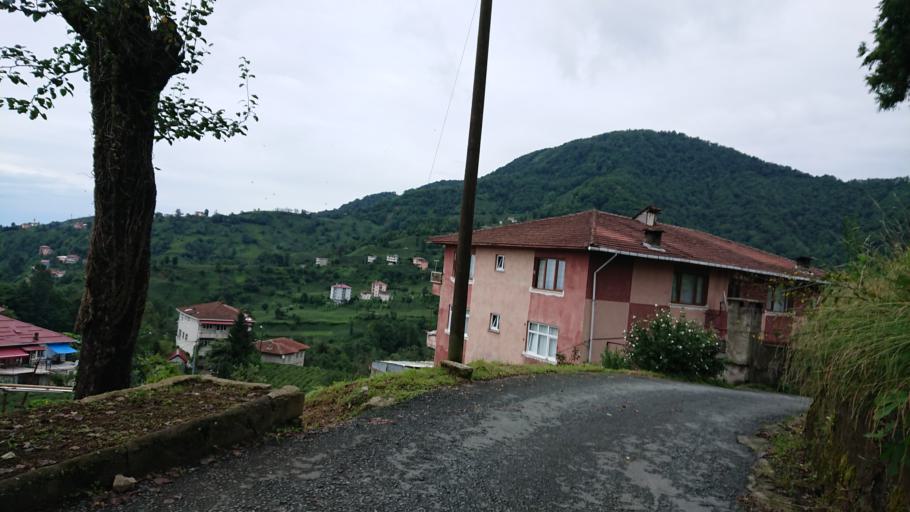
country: TR
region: Rize
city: Rize
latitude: 40.9812
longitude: 40.4850
